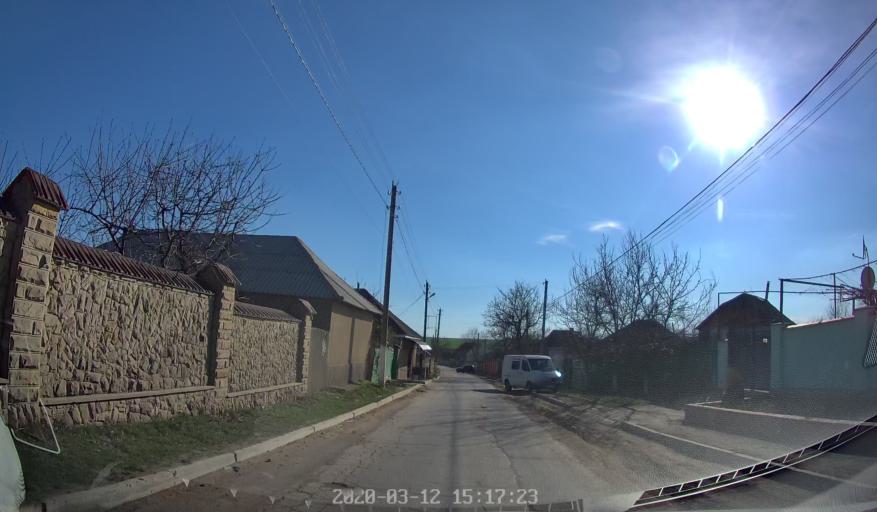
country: MD
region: Chisinau
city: Ciorescu
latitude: 47.2208
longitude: 28.9344
